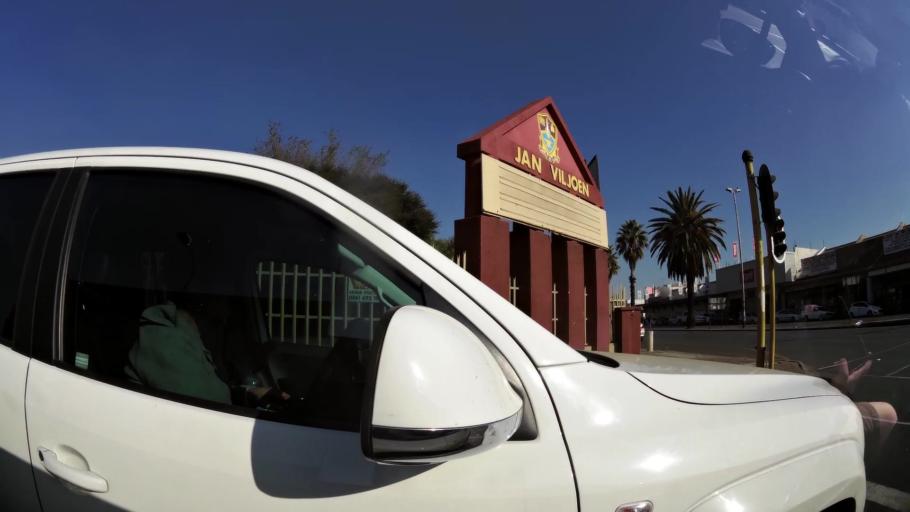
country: ZA
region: Gauteng
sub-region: West Rand District Municipality
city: Randfontein
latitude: -26.1822
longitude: 27.7039
